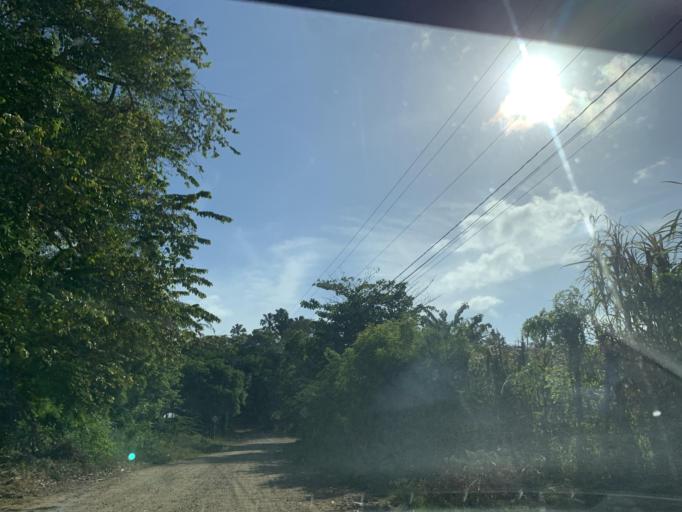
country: DO
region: Puerto Plata
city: Luperon
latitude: 19.8891
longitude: -70.8871
